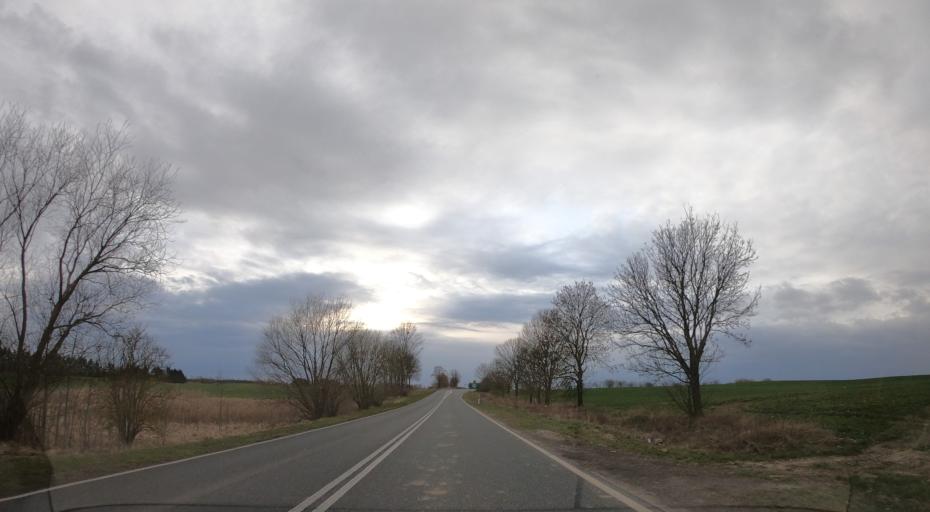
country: PL
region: West Pomeranian Voivodeship
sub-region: Powiat mysliborski
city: Nowogrodek Pomorski
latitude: 52.9036
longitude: 14.9796
